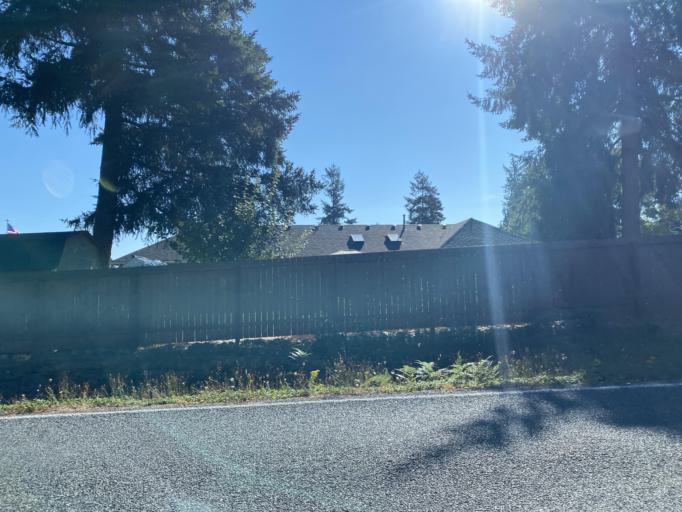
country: US
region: Washington
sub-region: Thurston County
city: Tanglewilde-Thompson Place
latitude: 47.0148
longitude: -122.7279
